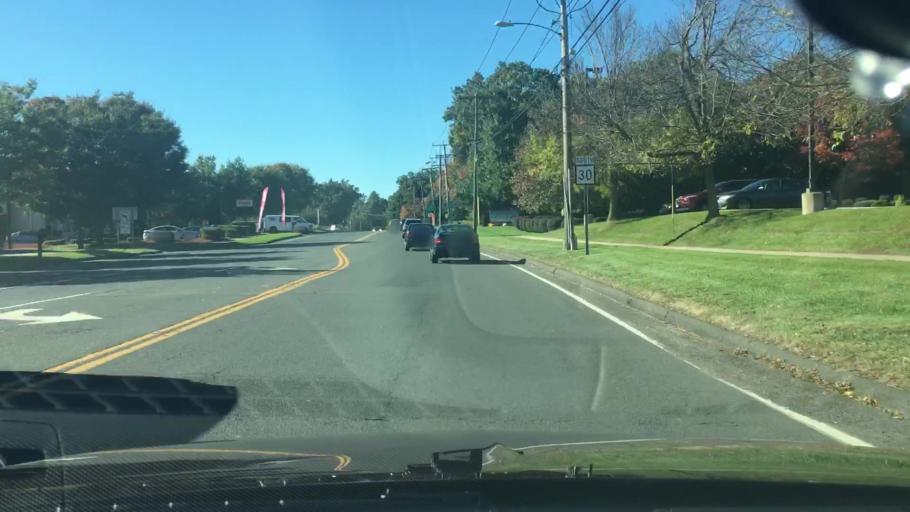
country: US
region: Connecticut
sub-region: Hartford County
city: Manchester
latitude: 41.8140
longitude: -72.5271
